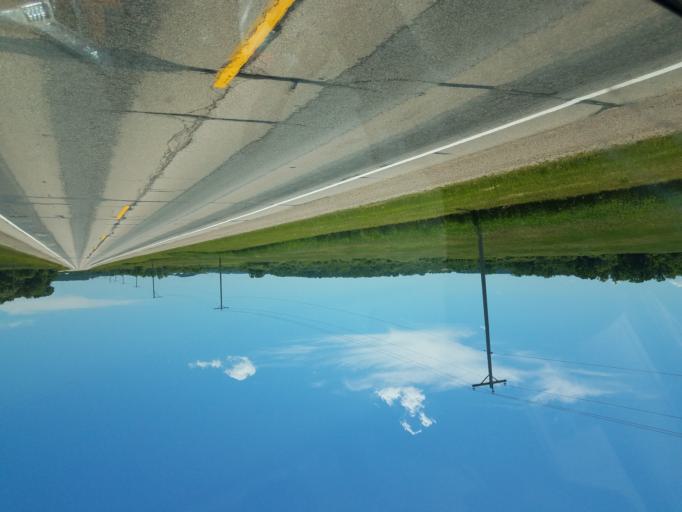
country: US
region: Wisconsin
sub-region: Juneau County
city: Elroy
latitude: 43.6796
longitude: -90.2776
